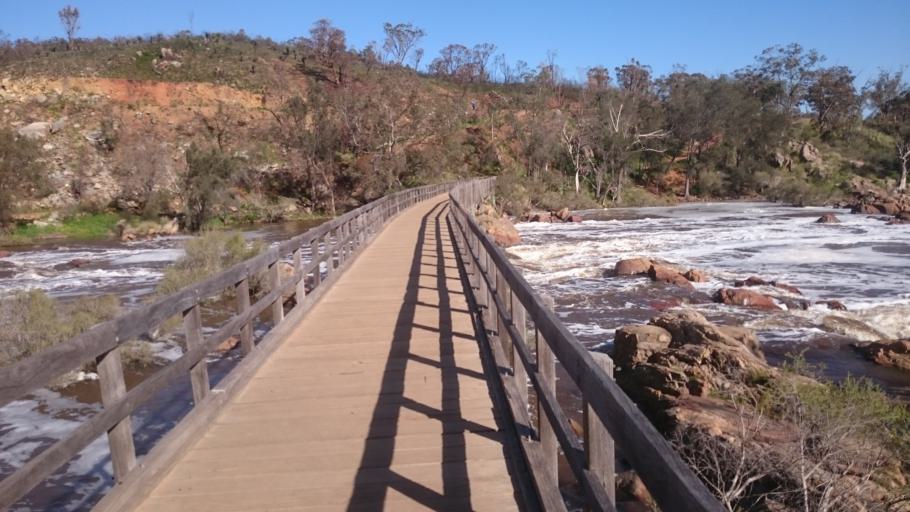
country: AU
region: Western Australia
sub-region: Swan
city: The Vines
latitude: -31.7724
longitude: 116.0626
